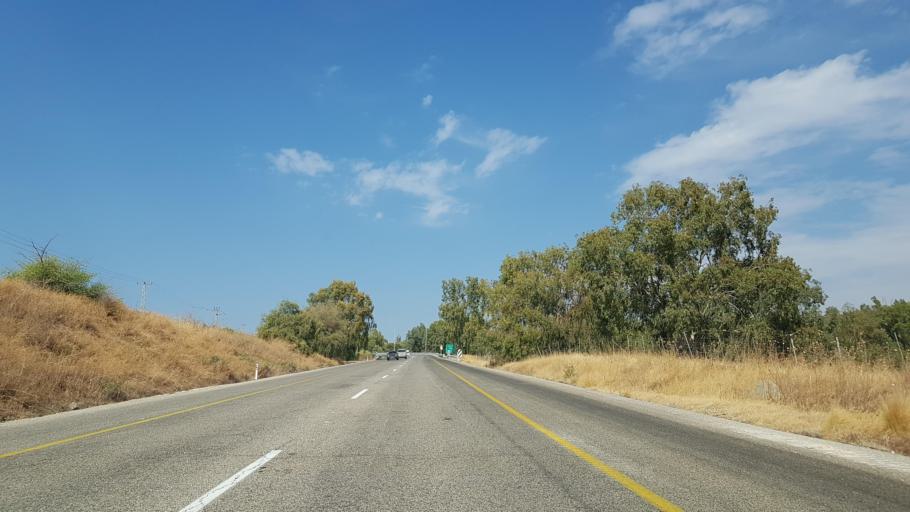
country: SY
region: Quneitra
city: Al Butayhah
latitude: 32.9087
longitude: 35.5974
